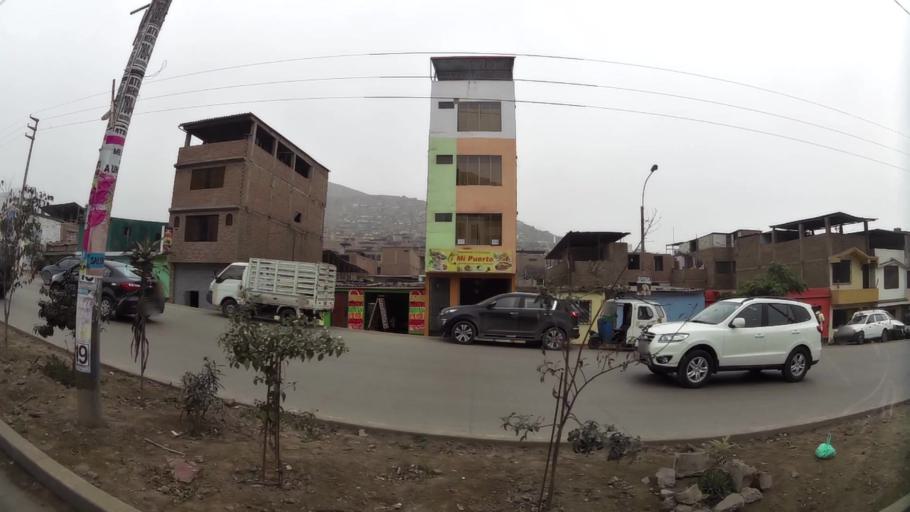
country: PE
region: Lima
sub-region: Lima
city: Surco
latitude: -12.1771
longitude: -76.9391
